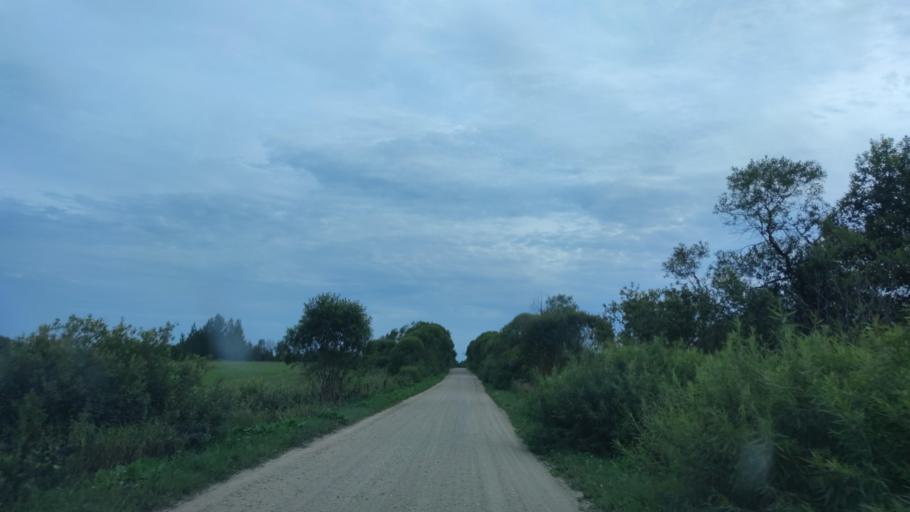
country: BY
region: Vitebsk
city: Mosar
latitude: 55.1238
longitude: 27.1554
